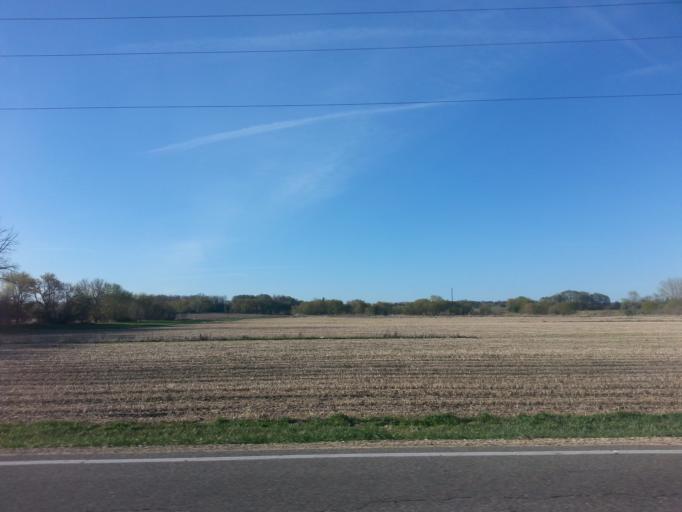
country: US
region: Minnesota
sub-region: Rice County
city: Northfield
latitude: 44.5437
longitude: -93.1445
